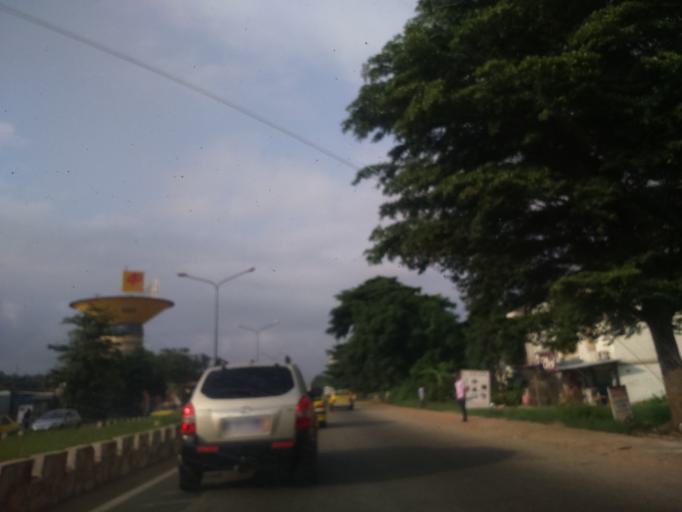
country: CI
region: Lagunes
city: Abidjan
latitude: 5.3396
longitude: -4.0036
